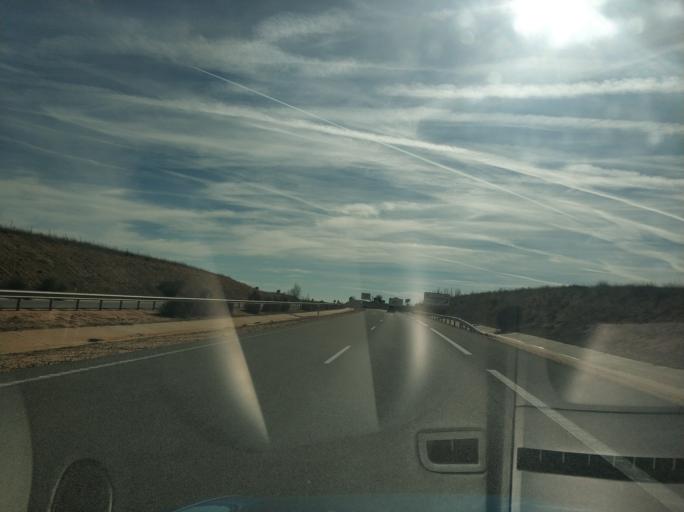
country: ES
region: Castille and Leon
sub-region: Provincia de Zamora
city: Cuelgamures
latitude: 41.2712
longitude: -5.7062
